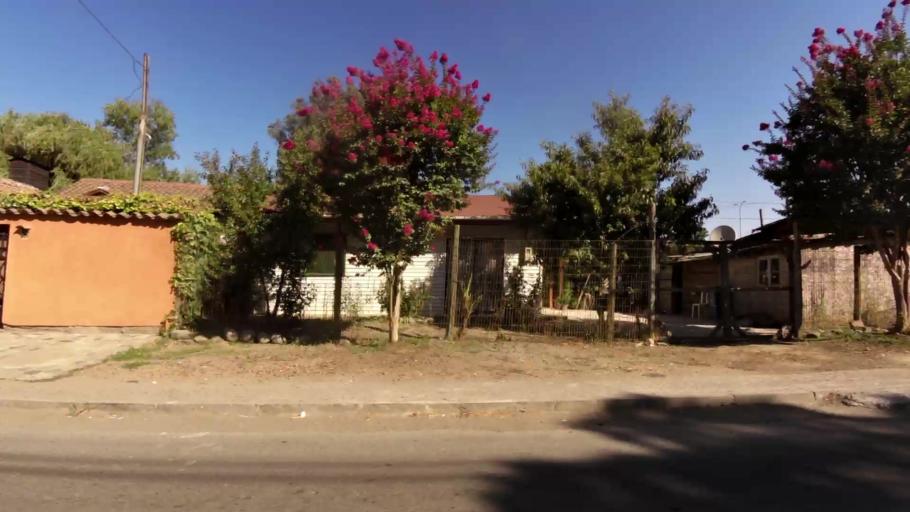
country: CL
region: Maule
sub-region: Provincia de Talca
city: Talca
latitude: -35.3988
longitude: -71.6264
